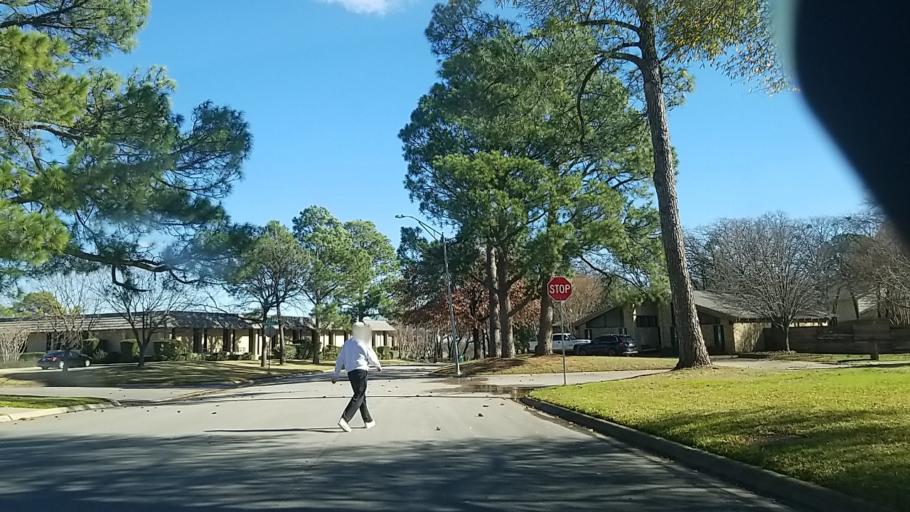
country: US
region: Texas
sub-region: Denton County
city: Denton
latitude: 33.1906
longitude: -97.1196
